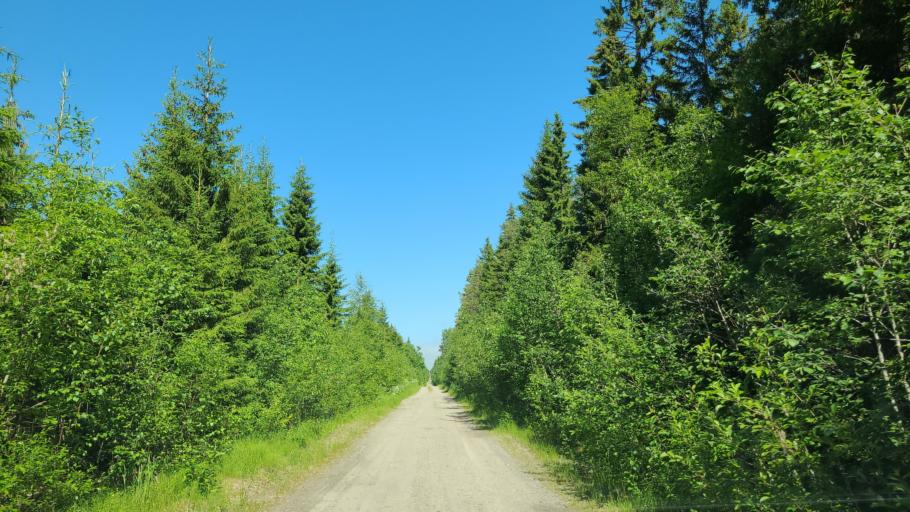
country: SE
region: Vaesternorrland
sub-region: OErnskoeldsviks Kommun
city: Husum
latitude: 63.4198
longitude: 19.2227
